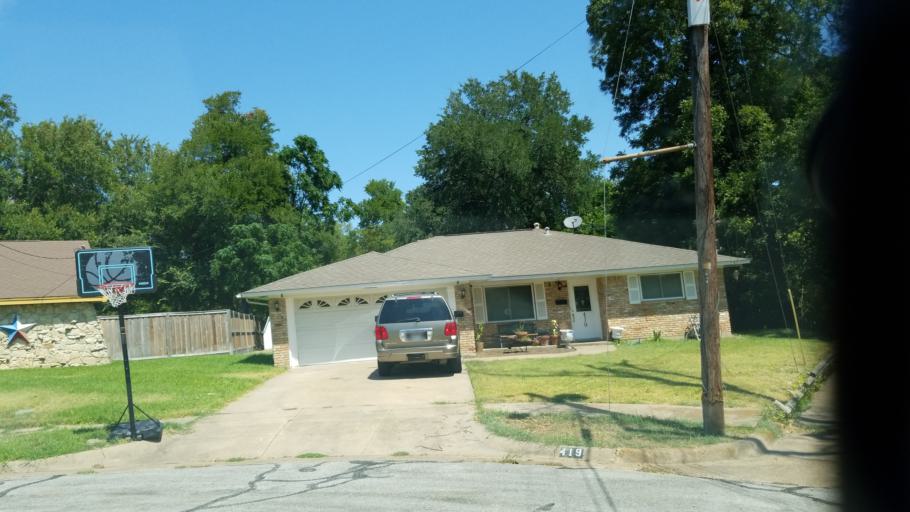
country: US
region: Texas
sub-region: Dallas County
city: Duncanville
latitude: 32.6530
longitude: -96.9013
